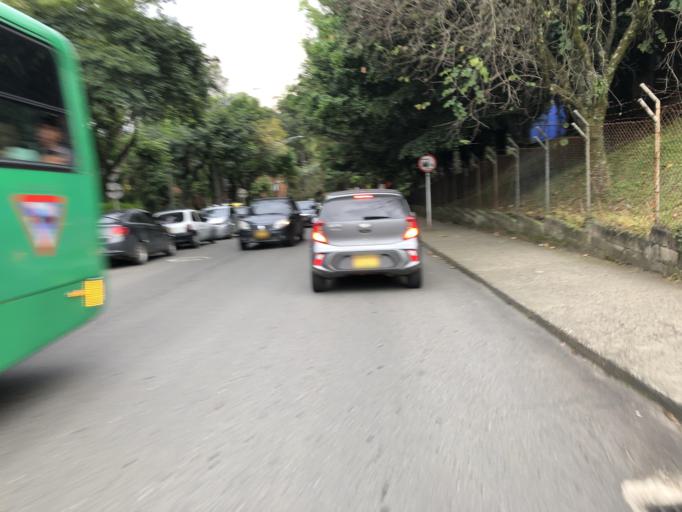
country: CO
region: Antioquia
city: Medellin
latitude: 6.2918
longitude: -75.5671
